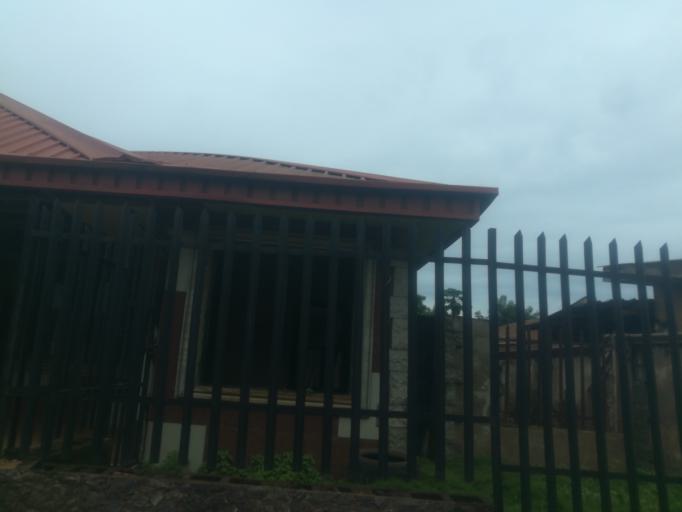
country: NG
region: Oyo
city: Ibadan
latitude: 7.3246
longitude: 3.8901
